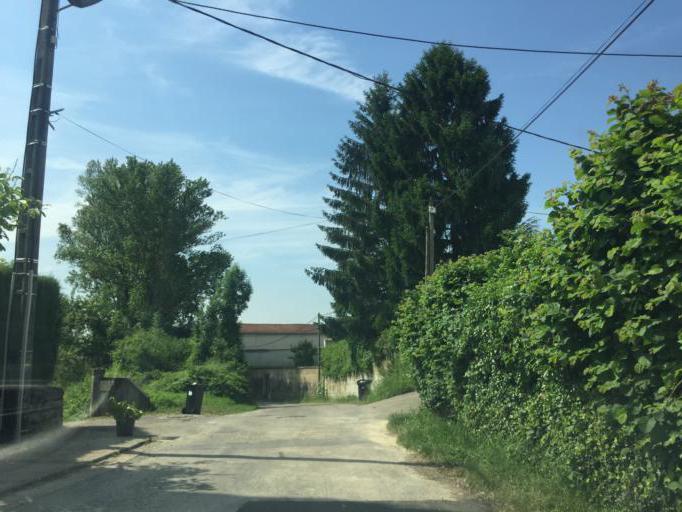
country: FR
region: Rhone-Alpes
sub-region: Departement de l'Ain
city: Miribel
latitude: 45.8230
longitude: 4.9309
